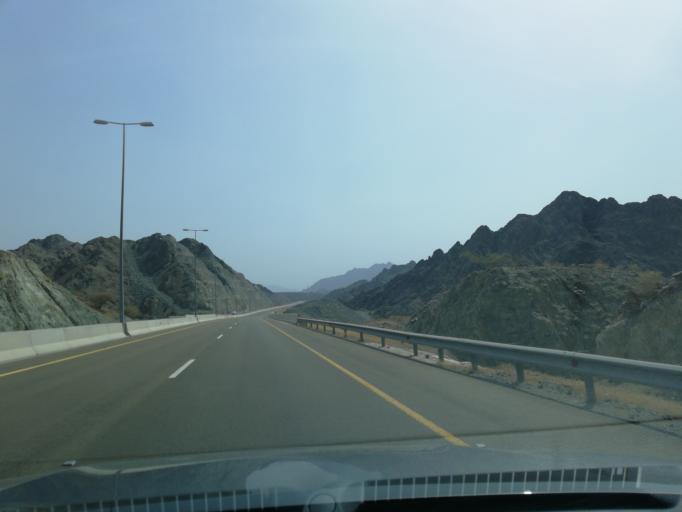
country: OM
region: Al Batinah
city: Al Liwa'
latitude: 24.2696
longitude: 56.3901
